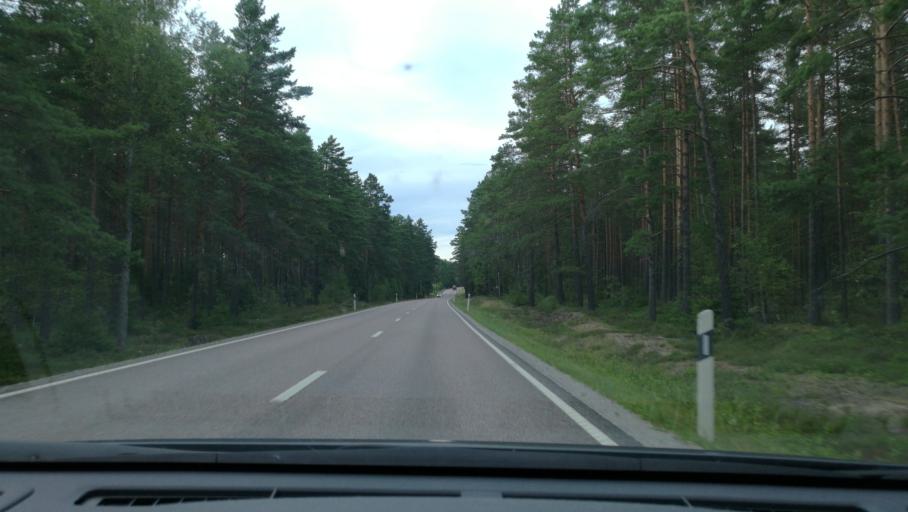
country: SE
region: Vaestmanland
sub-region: Kungsors Kommun
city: Kungsoer
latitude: 59.3228
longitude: 16.1102
